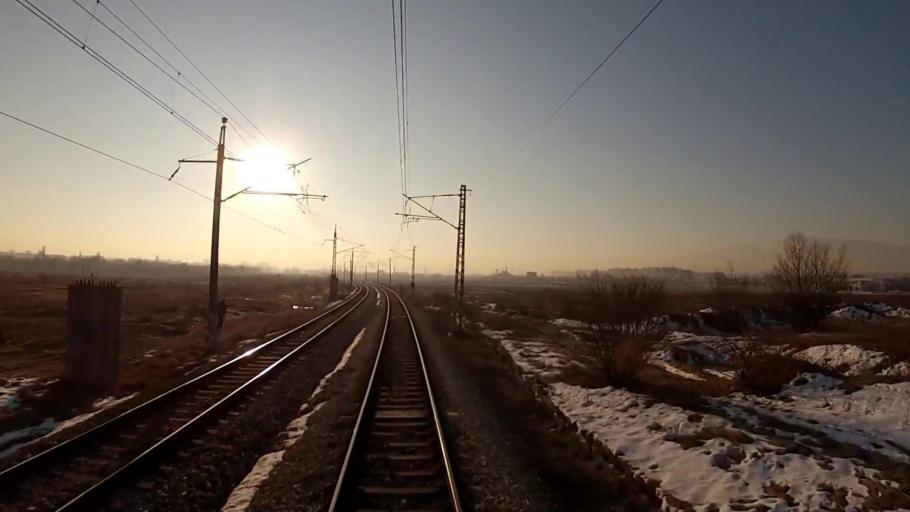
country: BG
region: Sofiya
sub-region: Obshtina Bozhurishte
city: Bozhurishte
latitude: 42.7433
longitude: 23.2585
